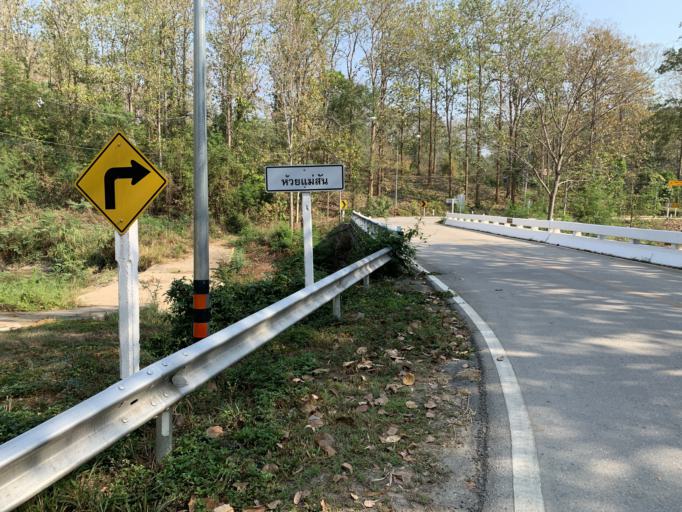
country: TH
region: Lampang
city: Hang Chat
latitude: 18.3582
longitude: 99.2557
